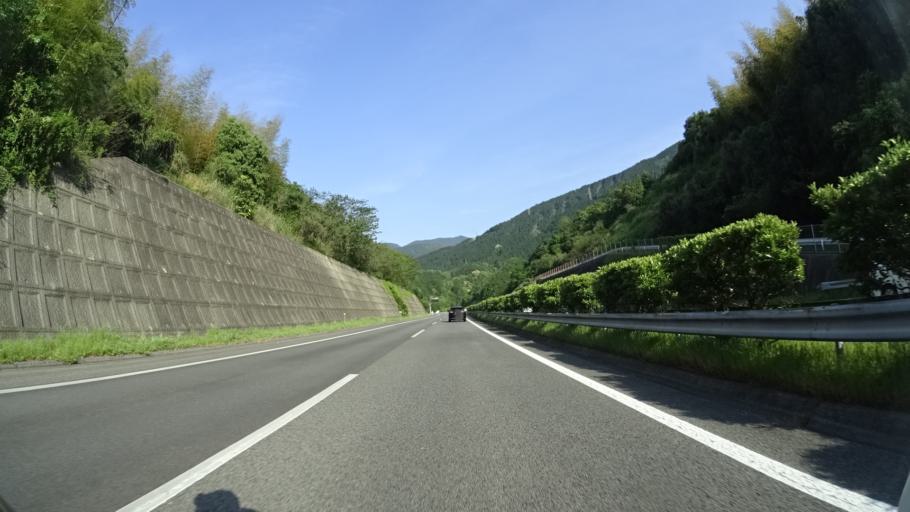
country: JP
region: Ehime
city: Saijo
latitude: 33.9107
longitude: 133.2475
